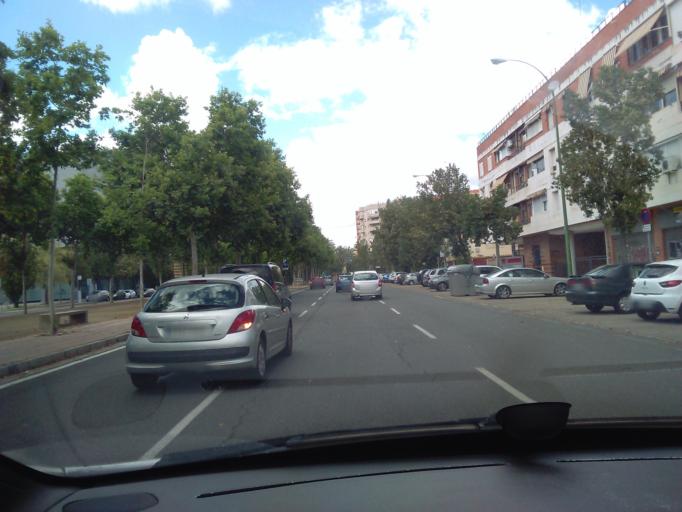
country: ES
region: Andalusia
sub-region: Provincia de Sevilla
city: Sevilla
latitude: 37.3727
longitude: -5.9765
